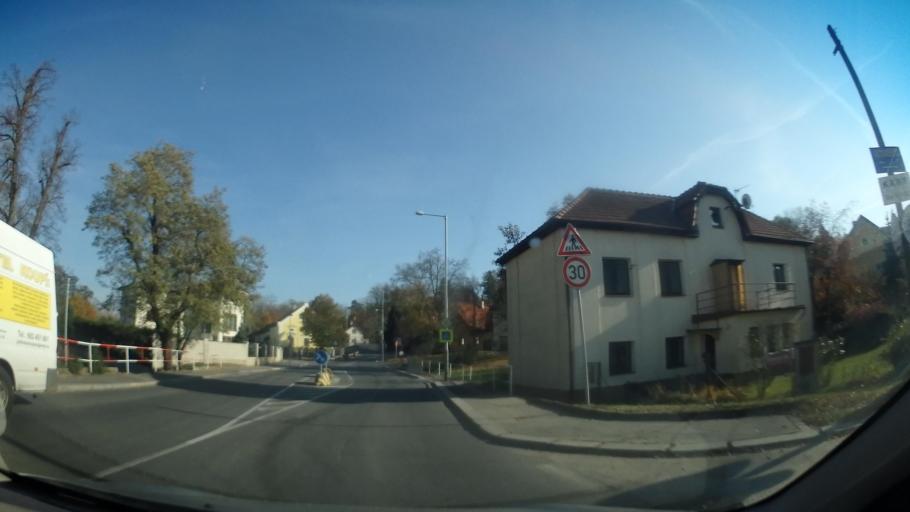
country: CZ
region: Praha
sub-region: Praha 14
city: Dolni Pocernice
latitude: 50.0619
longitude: 14.5964
